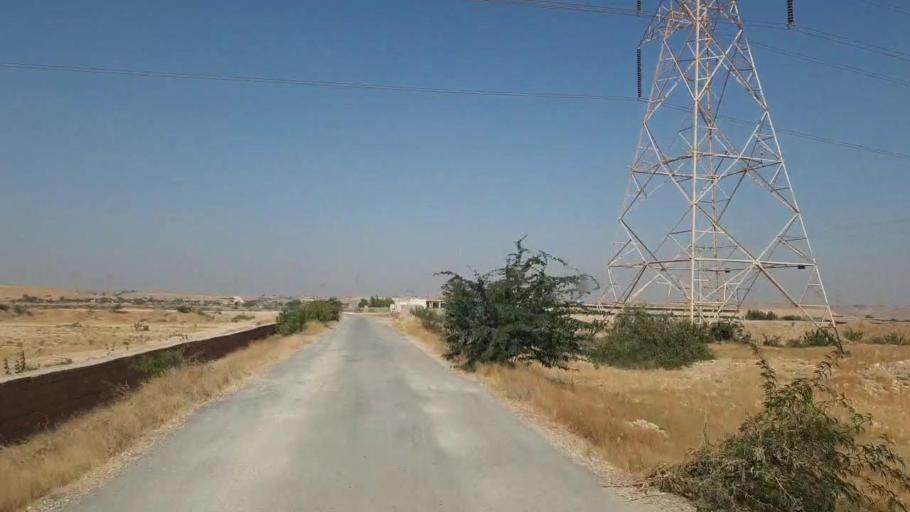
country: PK
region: Sindh
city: Thatta
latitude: 25.1881
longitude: 67.8040
